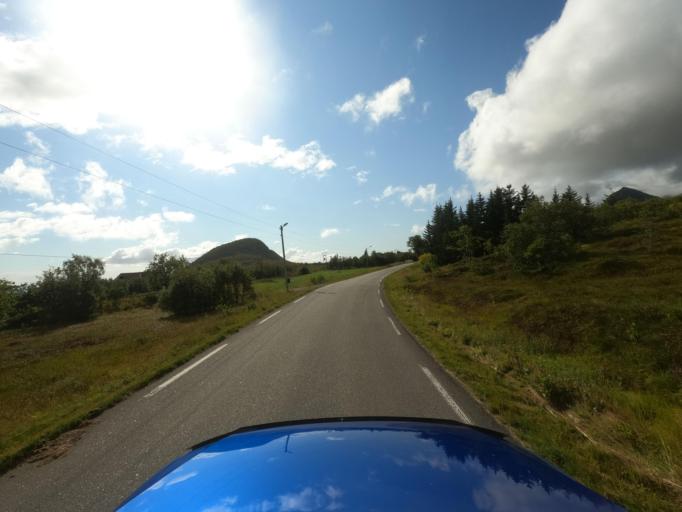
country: NO
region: Nordland
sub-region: Vagan
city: Kabelvag
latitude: 68.2351
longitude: 14.1146
